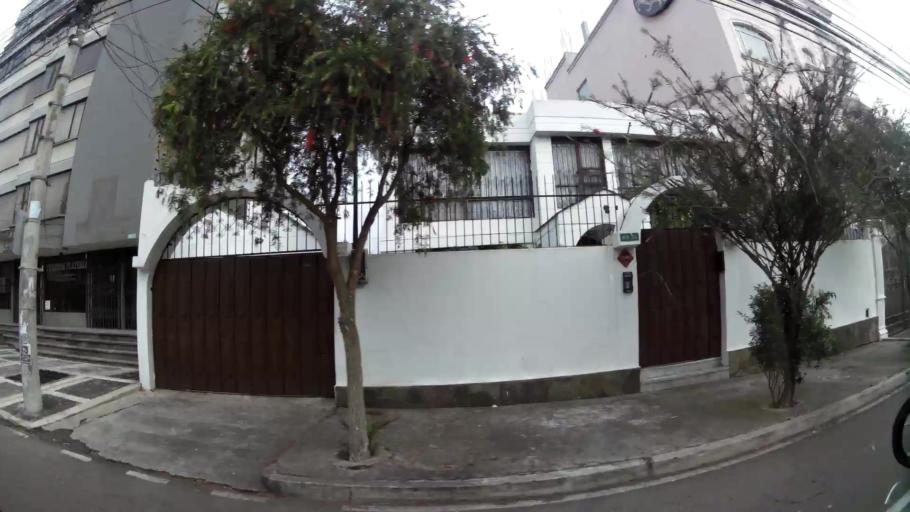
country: EC
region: Pichincha
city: Quito
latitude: -0.1987
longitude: -78.4869
